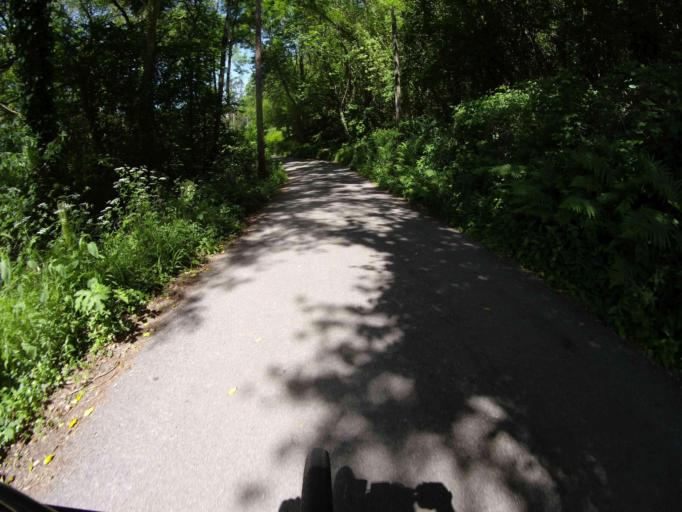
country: GB
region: England
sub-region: Devon
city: Bovey Tracey
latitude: 50.6135
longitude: -3.7115
